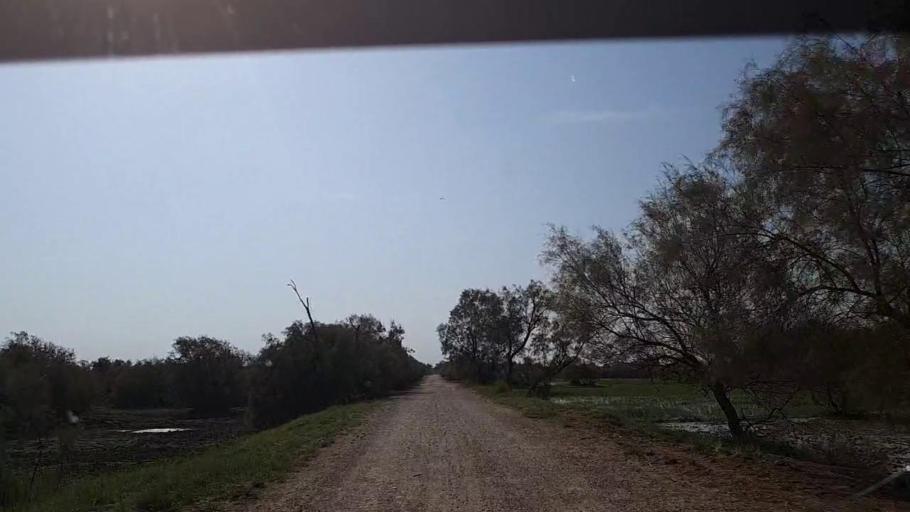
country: PK
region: Sindh
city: Khanpur
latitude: 27.8387
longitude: 69.3176
